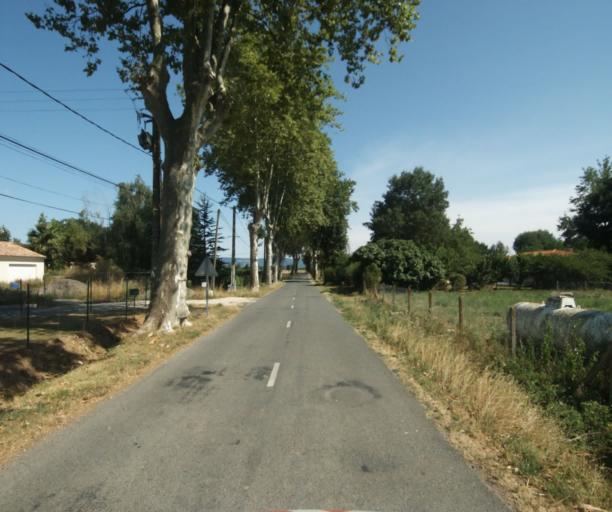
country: FR
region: Midi-Pyrenees
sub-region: Departement de la Haute-Garonne
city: Revel
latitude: 43.4941
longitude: 1.9701
